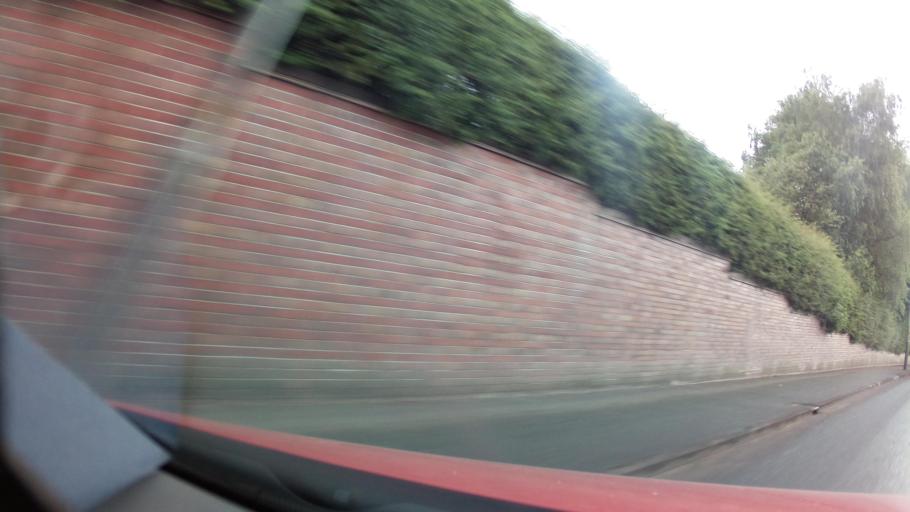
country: GB
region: England
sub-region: Wolverhampton
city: Wolverhampton
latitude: 52.5574
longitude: -2.1658
